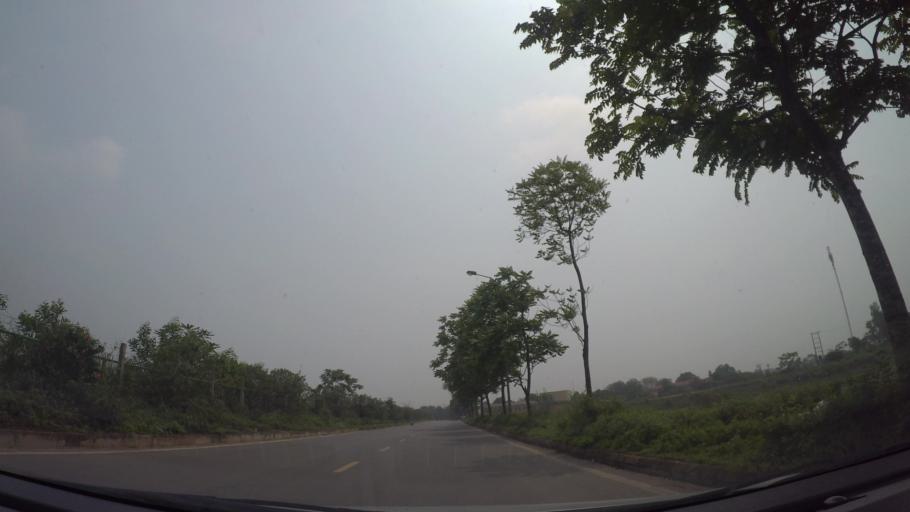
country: VN
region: Ha Noi
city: Quoc Oai
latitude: 20.9962
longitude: 105.5930
